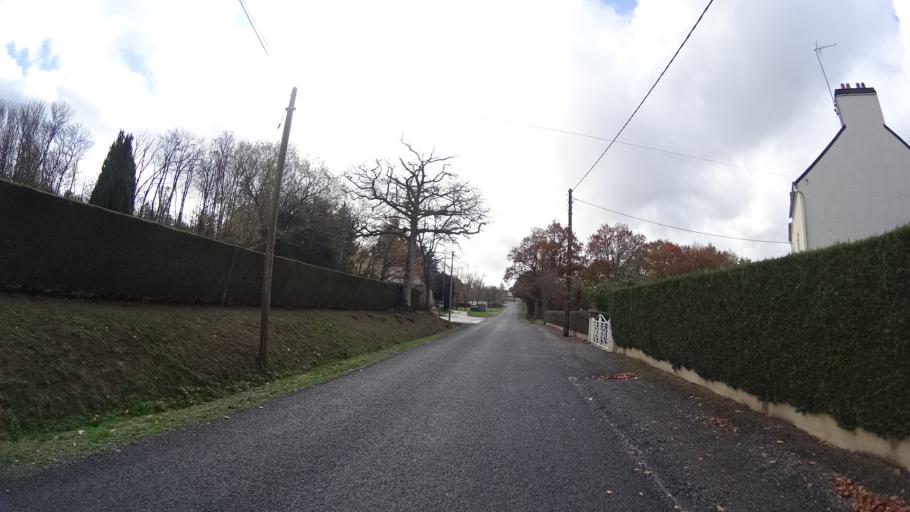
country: FR
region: Pays de la Loire
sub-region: Departement de la Loire-Atlantique
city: Fegreac
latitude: 47.6009
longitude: -2.0664
